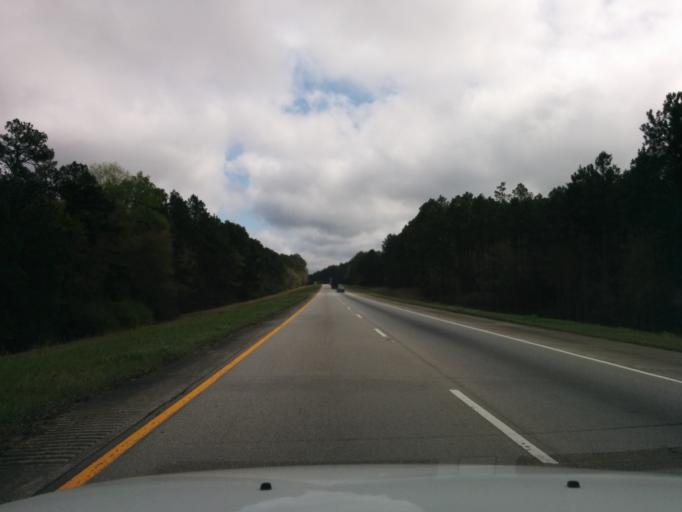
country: US
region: Georgia
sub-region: Emanuel County
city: Swainsboro
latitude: 32.4130
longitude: -82.3733
